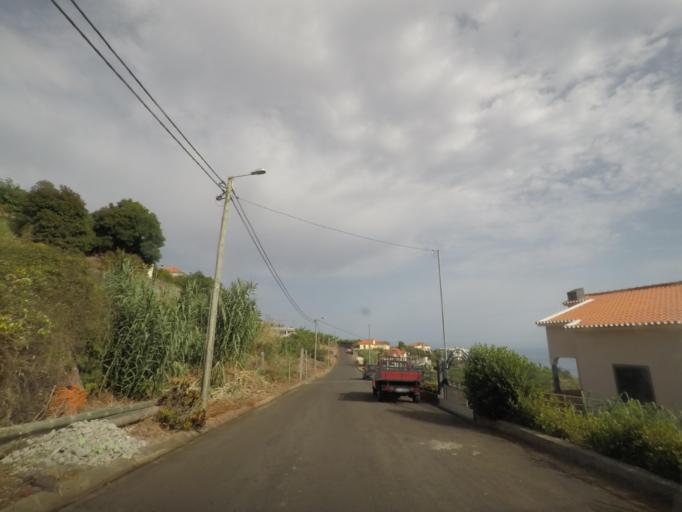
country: PT
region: Madeira
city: Ponta do Sol
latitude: 32.6947
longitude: -17.1190
